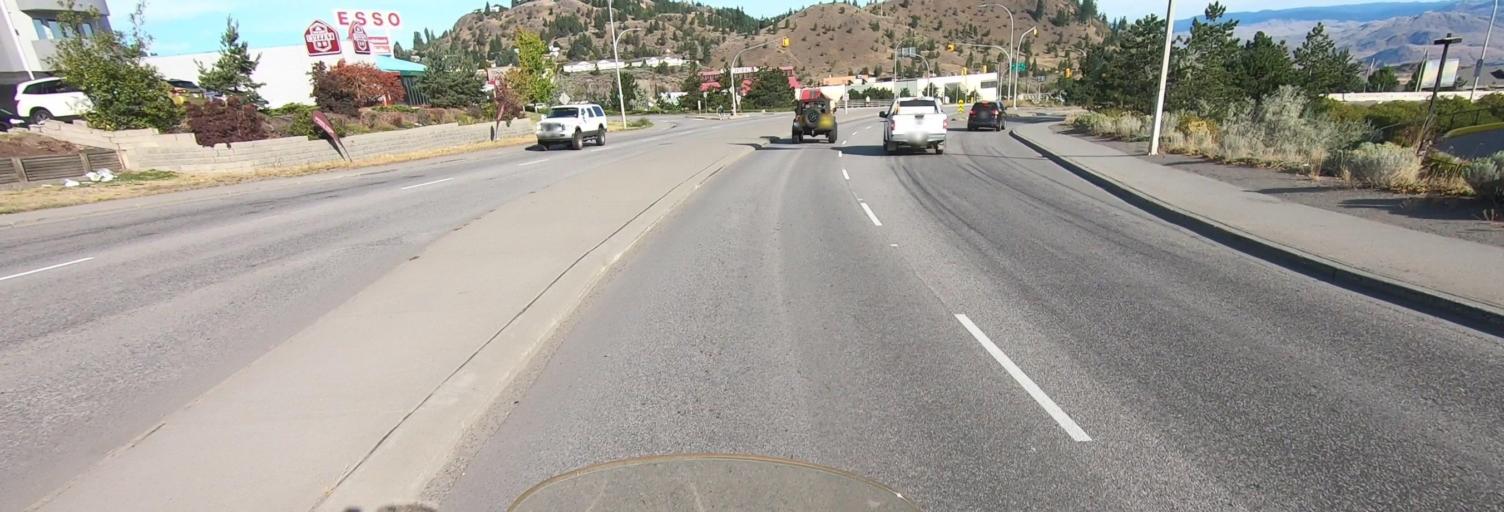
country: CA
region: British Columbia
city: Kamloops
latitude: 50.6526
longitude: -120.3677
